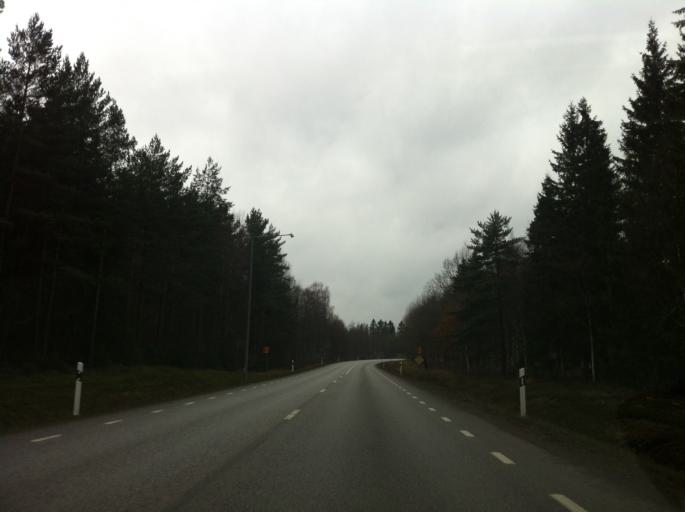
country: SE
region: Joenkoeping
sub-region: Vetlanda Kommun
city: Vetlanda
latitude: 57.4126
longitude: 15.0793
